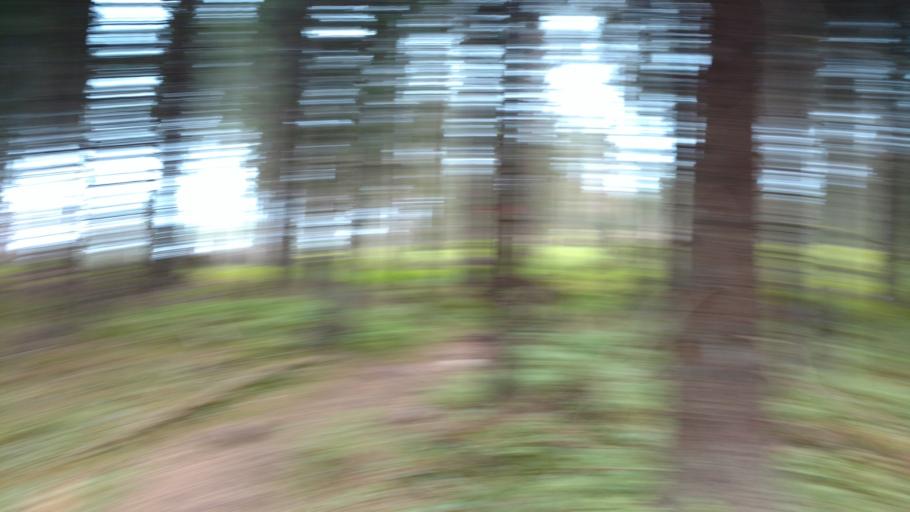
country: FI
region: Uusimaa
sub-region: Raaseporin
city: Pohja
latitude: 60.1170
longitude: 23.5620
